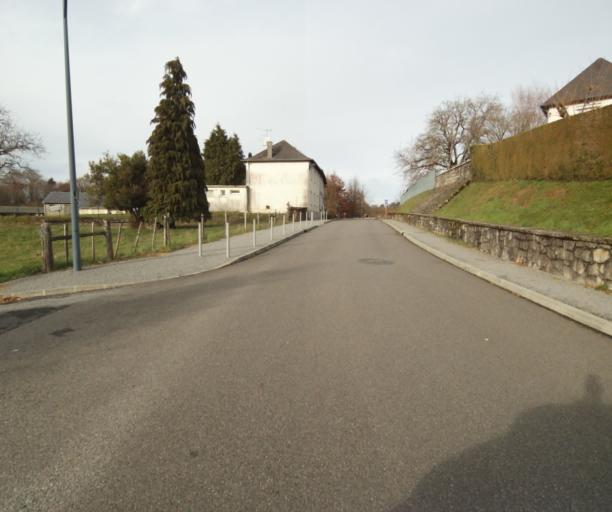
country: FR
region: Limousin
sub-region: Departement de la Correze
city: Saint-Mexant
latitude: 45.2633
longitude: 1.6773
